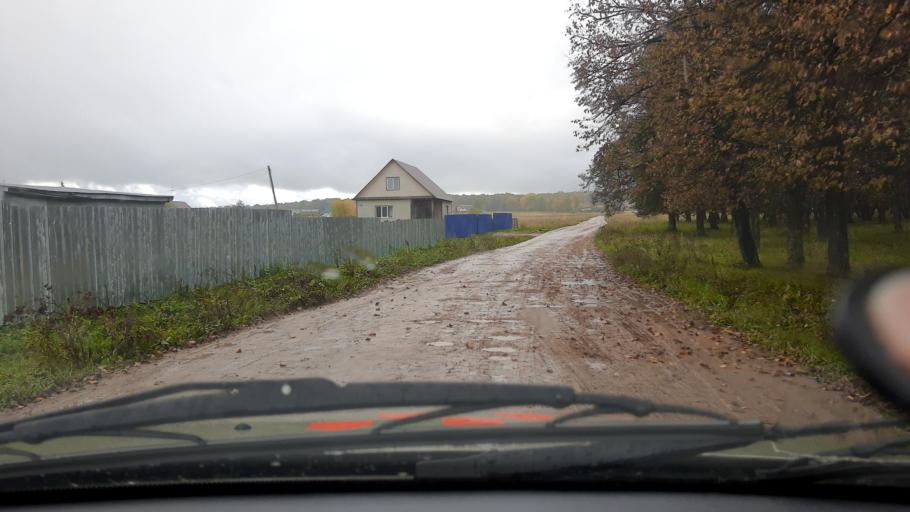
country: RU
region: Bashkortostan
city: Kudeyevskiy
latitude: 54.8805
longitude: 56.6329
